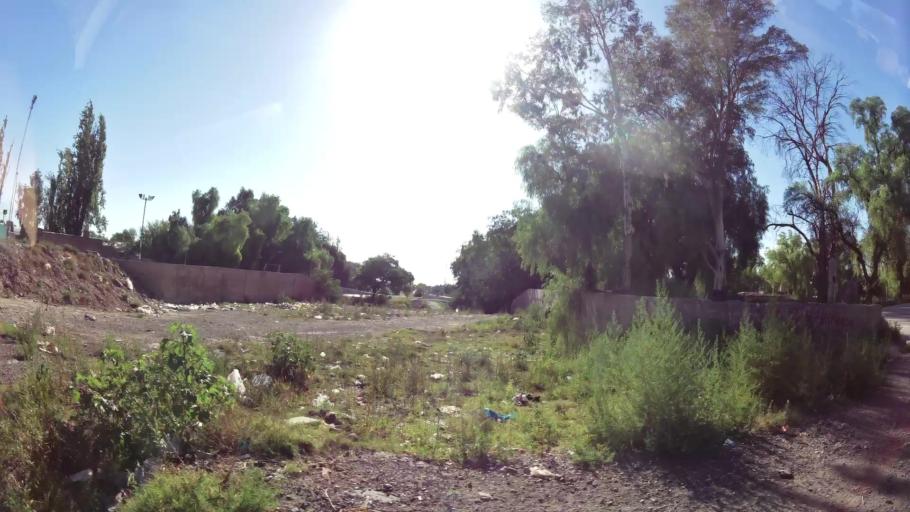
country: AR
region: Mendoza
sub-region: Departamento de Godoy Cruz
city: Godoy Cruz
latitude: -32.9257
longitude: -68.8689
